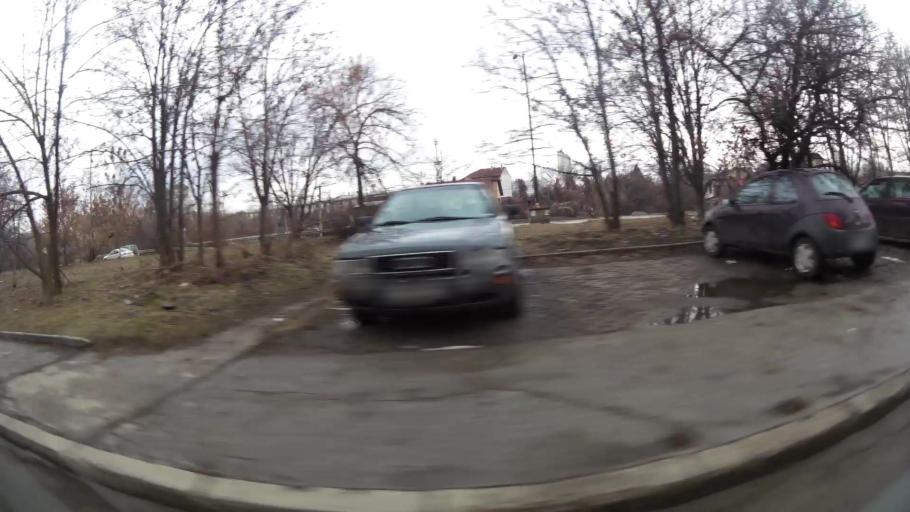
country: BG
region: Sofia-Capital
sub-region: Stolichna Obshtina
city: Sofia
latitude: 42.7236
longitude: 23.2979
